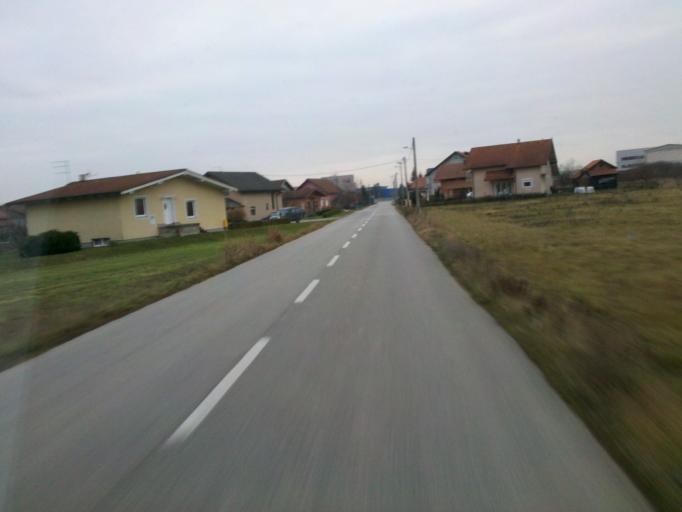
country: HR
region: Grad Zagreb
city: Lucko
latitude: 45.7570
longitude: 15.8752
